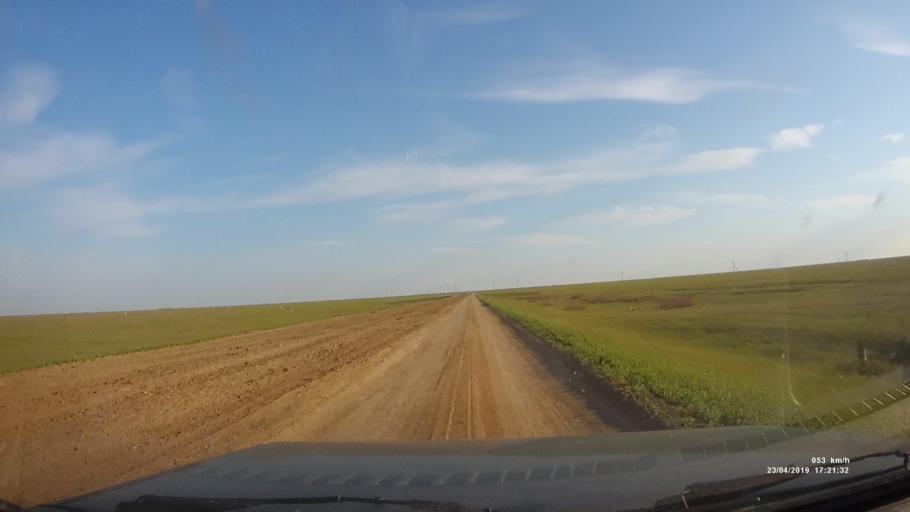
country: RU
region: Kalmykiya
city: Priyutnoye
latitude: 46.1754
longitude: 43.5054
